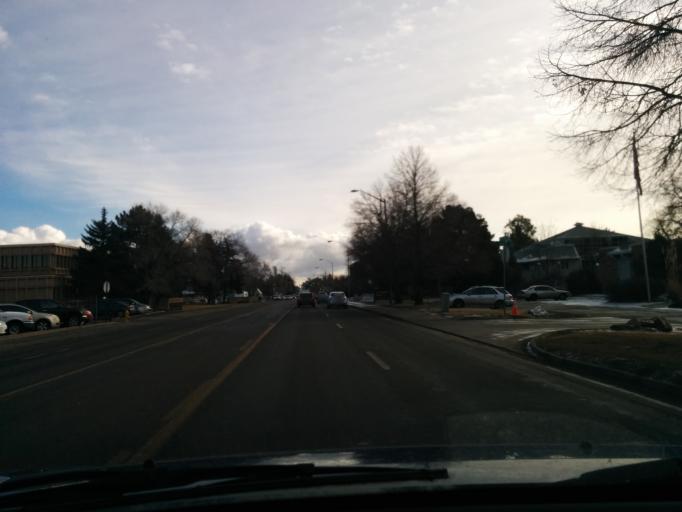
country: US
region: Colorado
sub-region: Larimer County
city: Fort Collins
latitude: 40.5671
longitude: -105.0821
